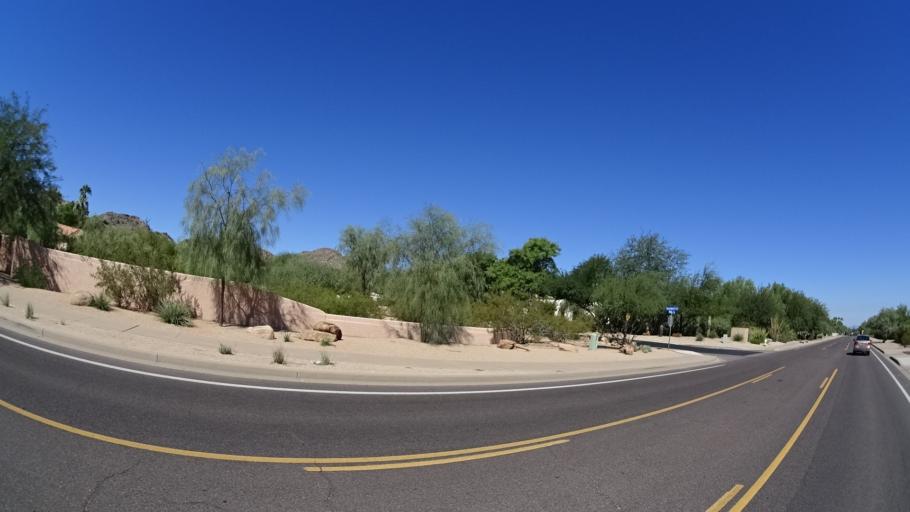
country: US
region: Arizona
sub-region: Maricopa County
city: Paradise Valley
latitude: 33.5437
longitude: -111.9347
